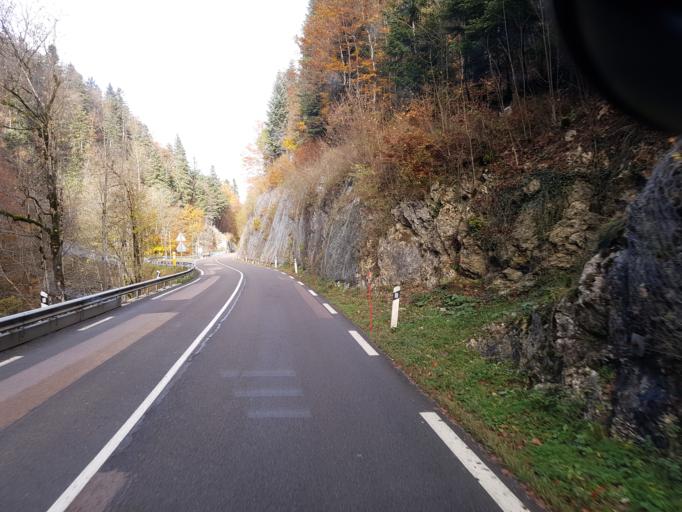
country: FR
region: Franche-Comte
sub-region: Departement du Jura
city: Champagnole
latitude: 46.6679
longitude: 5.9400
